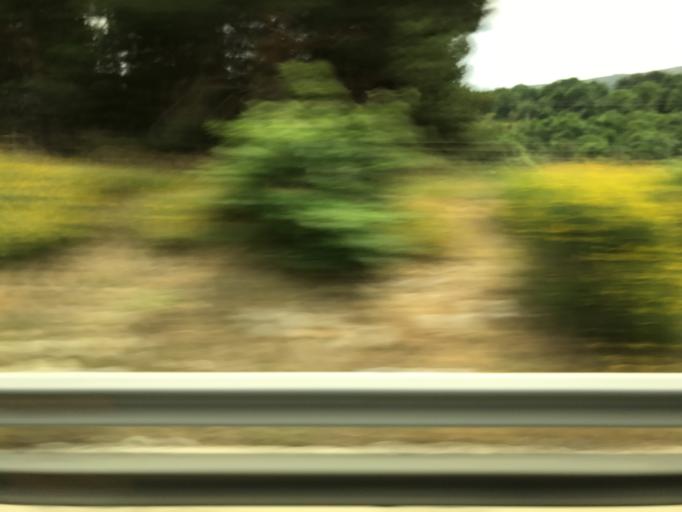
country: ES
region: Madrid
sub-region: Provincia de Madrid
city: Somosierra
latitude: 41.1275
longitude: -3.5831
